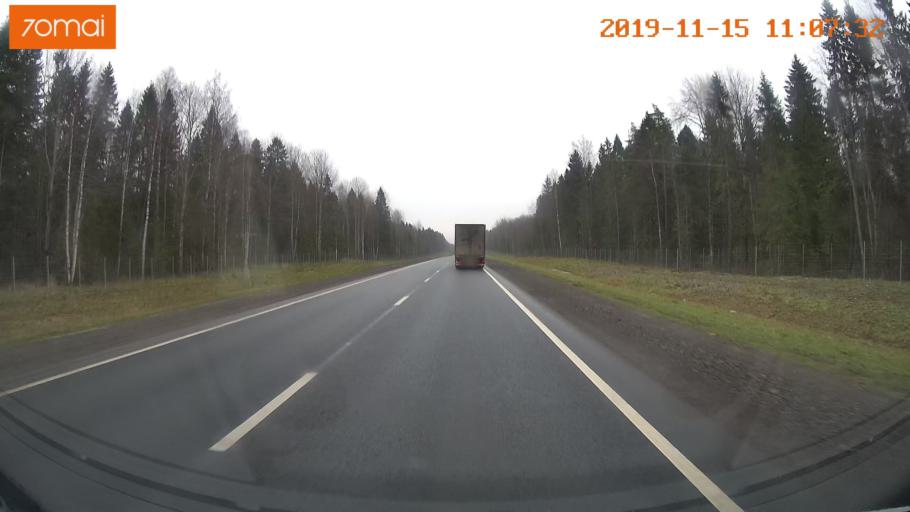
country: RU
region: Vologda
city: Chebsara
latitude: 59.1195
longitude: 39.0525
